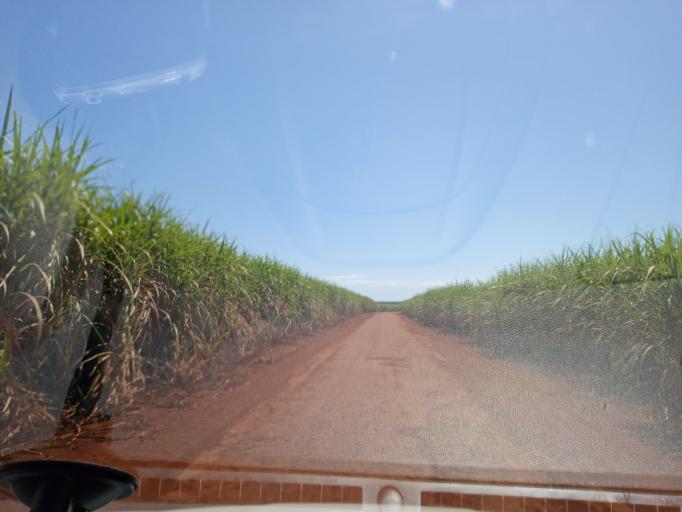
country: BR
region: Goias
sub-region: Itumbiara
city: Itumbiara
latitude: -18.4434
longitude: -49.1502
